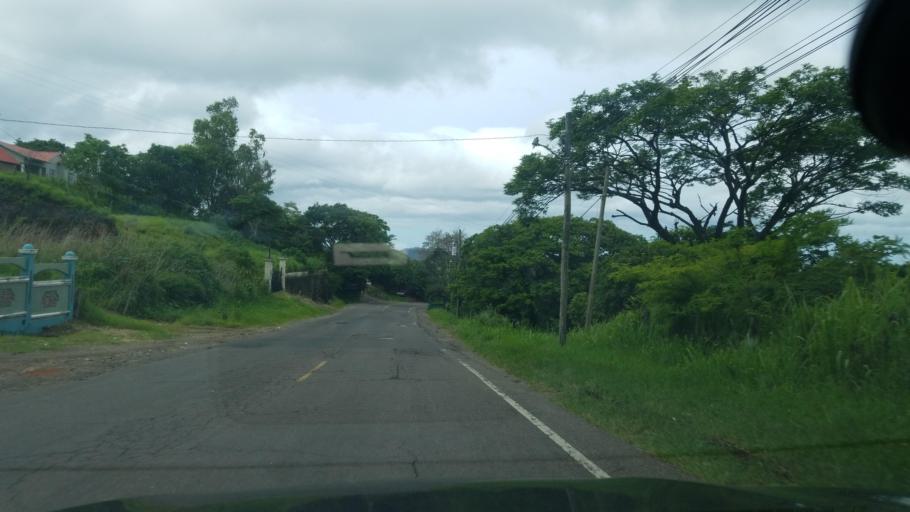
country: HN
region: Choluteca
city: Corpus
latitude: 13.3685
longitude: -86.9736
